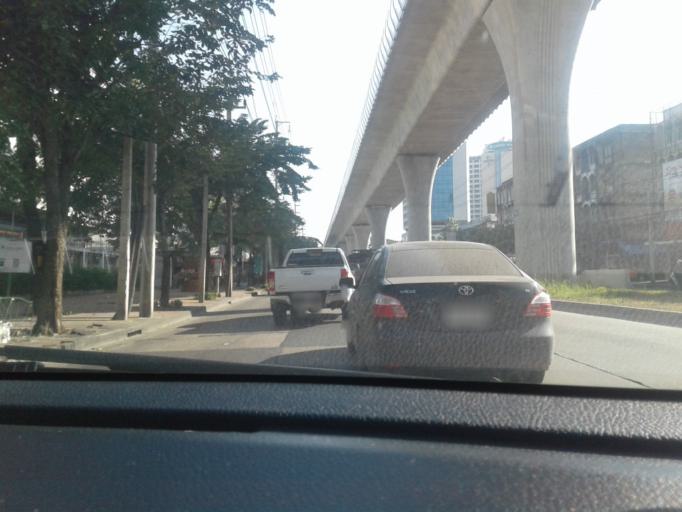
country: TH
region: Bangkok
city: Bangkok Yai
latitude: 13.7221
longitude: 100.4603
